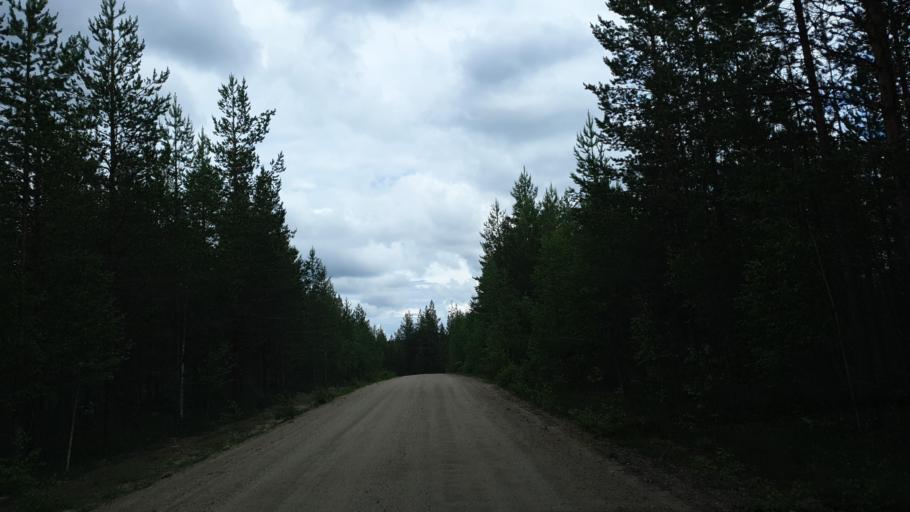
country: SE
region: Jaemtland
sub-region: Harjedalens Kommun
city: Sveg
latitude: 62.0449
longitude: 14.4798
